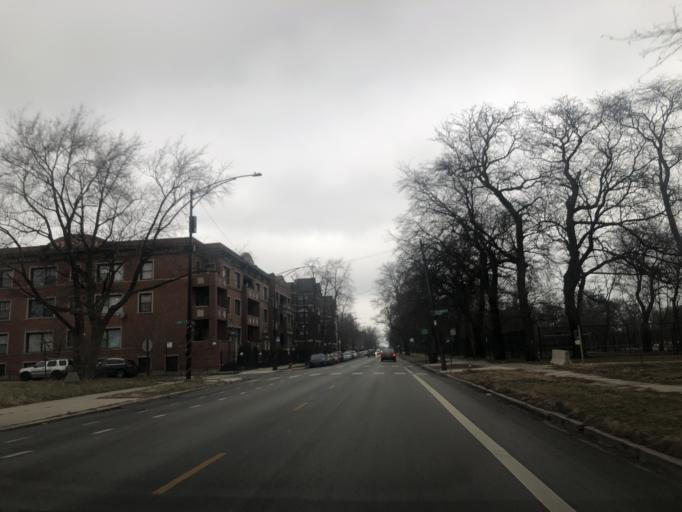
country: US
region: Illinois
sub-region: Cook County
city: Chicago
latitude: 41.7888
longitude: -87.6158
